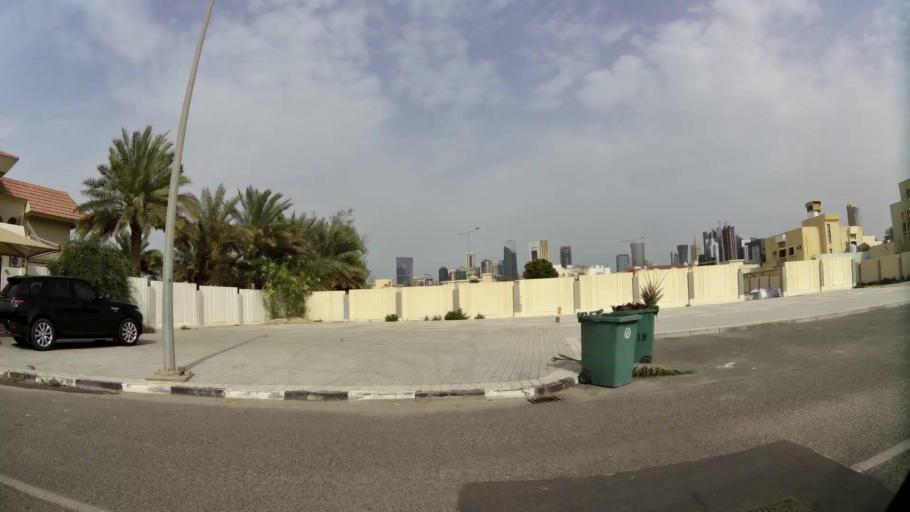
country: QA
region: Baladiyat ad Dawhah
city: Doha
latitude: 25.3253
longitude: 51.5080
